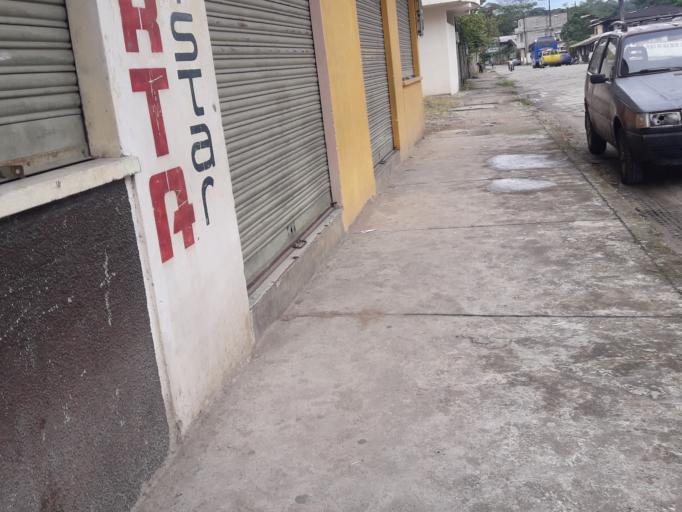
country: EC
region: Napo
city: Tena
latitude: -0.9994
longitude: -77.8149
